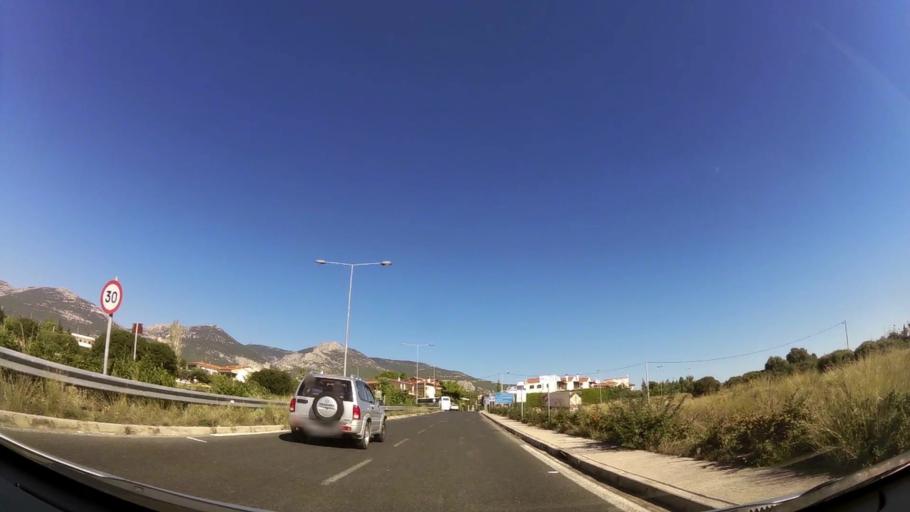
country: GR
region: Attica
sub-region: Nomarchia Anatolikis Attikis
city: Thrakomakedones
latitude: 38.1186
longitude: 23.7621
